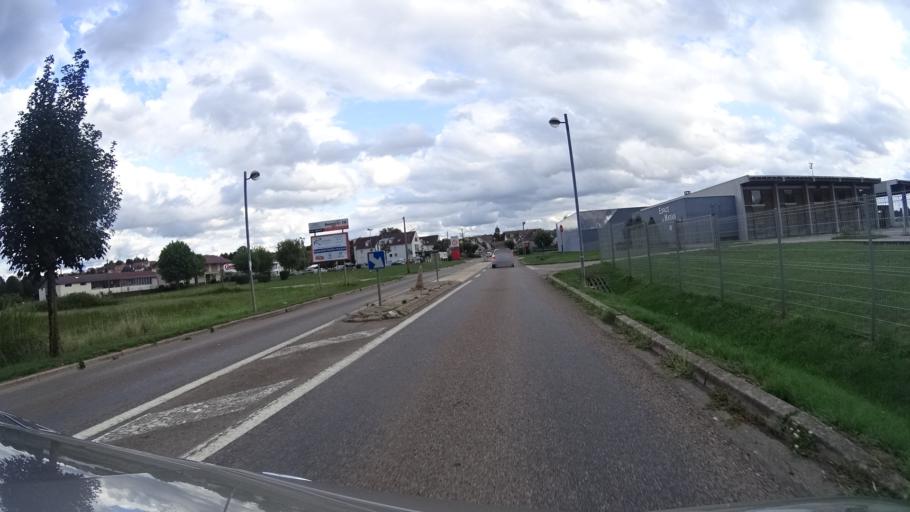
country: FR
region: Franche-Comte
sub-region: Departement du Doubs
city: Saone
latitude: 47.2290
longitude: 6.1126
